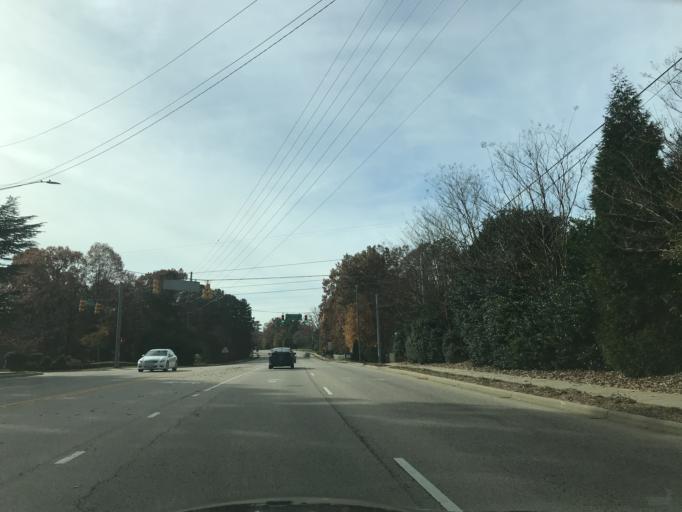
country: US
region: North Carolina
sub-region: Wake County
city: West Raleigh
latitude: 35.8356
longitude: -78.6942
